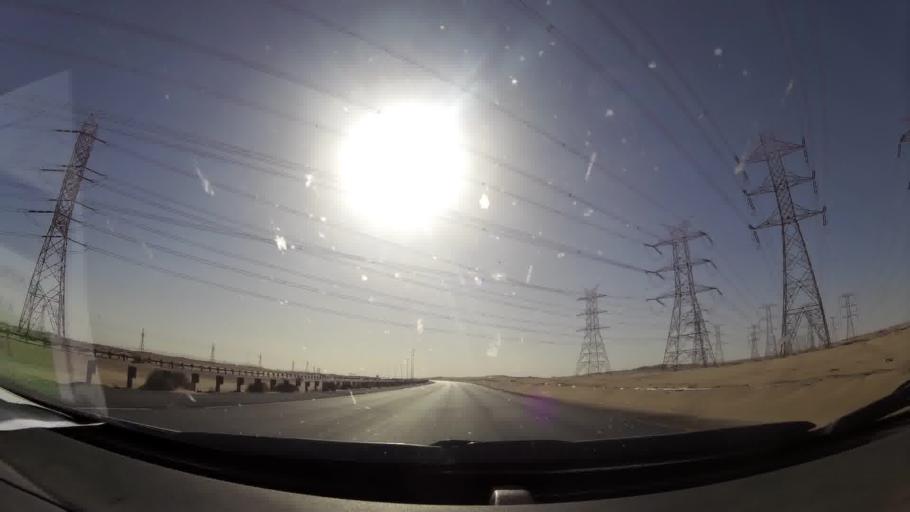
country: KW
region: Al Asimah
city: Kuwait City
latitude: 29.6261
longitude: 47.9237
